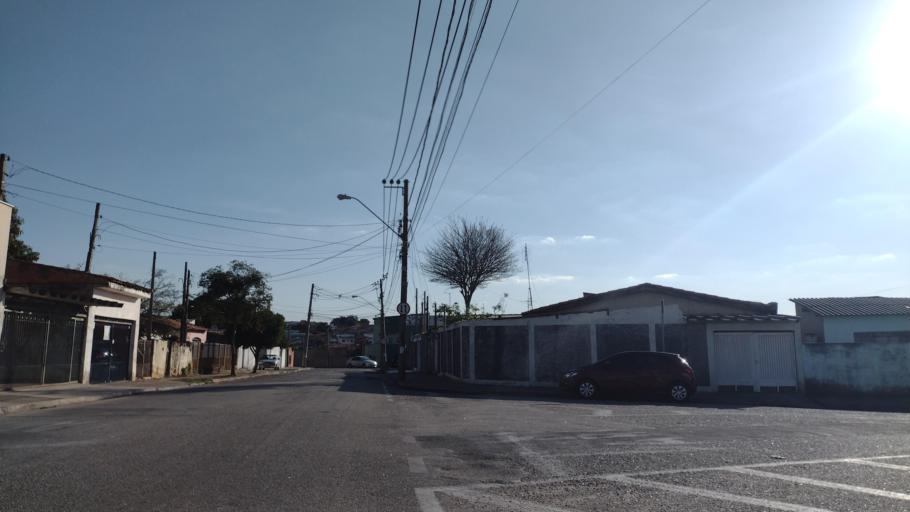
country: BR
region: Sao Paulo
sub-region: Sorocaba
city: Sorocaba
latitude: -23.4732
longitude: -47.4792
